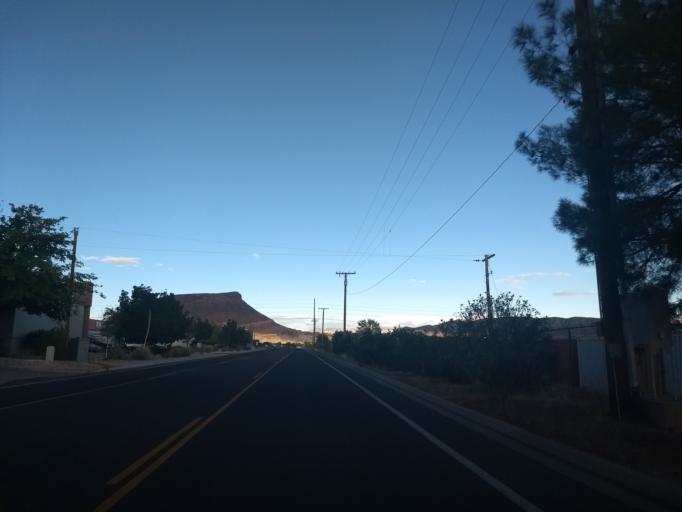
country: US
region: Utah
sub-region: Washington County
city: Washington
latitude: 37.1151
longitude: -113.5105
